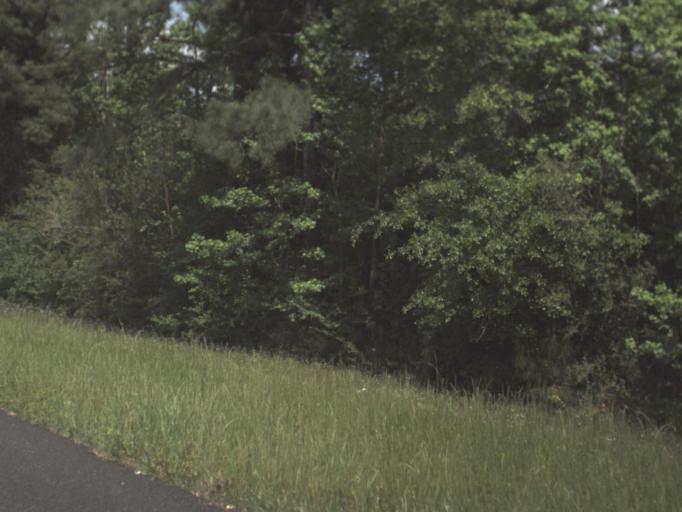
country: US
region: Florida
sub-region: Escambia County
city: Molino
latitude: 30.8404
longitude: -87.3258
